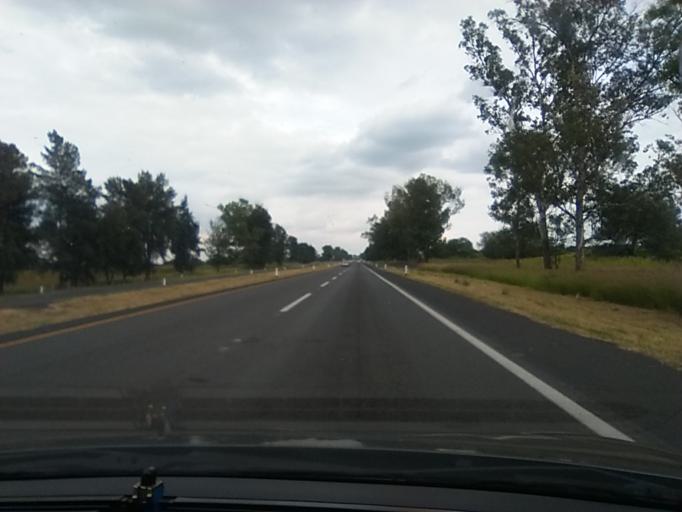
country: MX
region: Jalisco
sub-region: Ocotlan
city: Joconoxtle (La Tuna)
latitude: 20.3773
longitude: -102.6797
